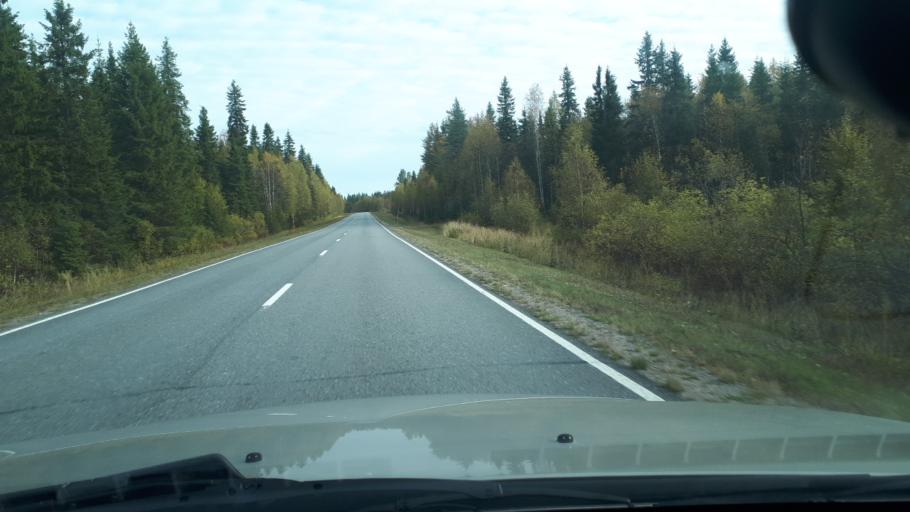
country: FI
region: Lapland
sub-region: Rovaniemi
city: Rovaniemi
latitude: 65.9565
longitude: 25.9352
